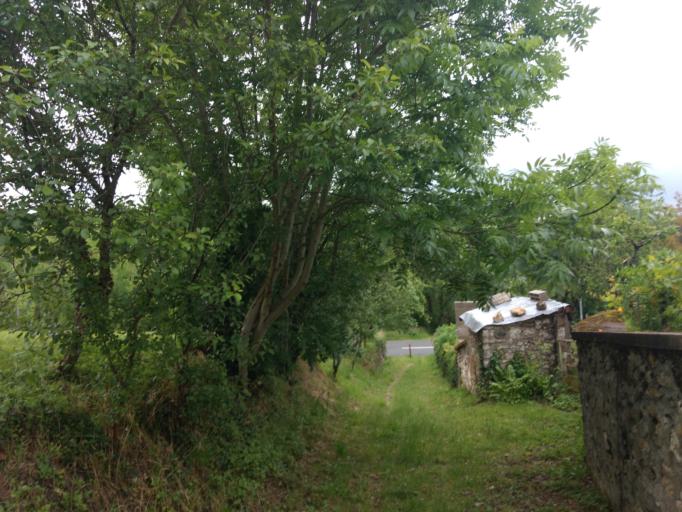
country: FR
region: Midi-Pyrenees
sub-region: Departement de l'Aveyron
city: Viviez
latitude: 44.5462
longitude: 2.1475
